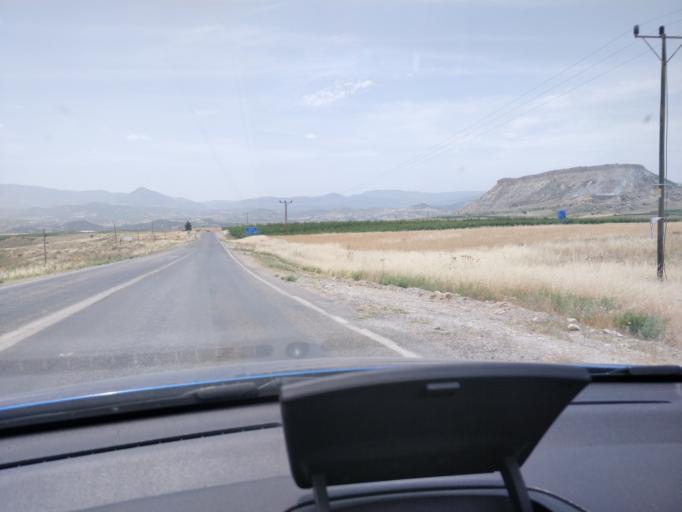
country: TR
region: Mersin
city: Mut
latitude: 36.6007
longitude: 33.4346
